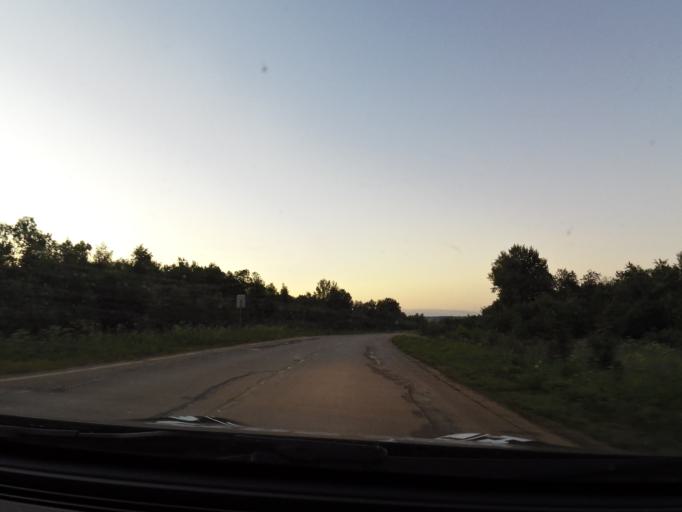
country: RU
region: Vologda
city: Vytegra
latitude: 60.9050
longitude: 36.0442
